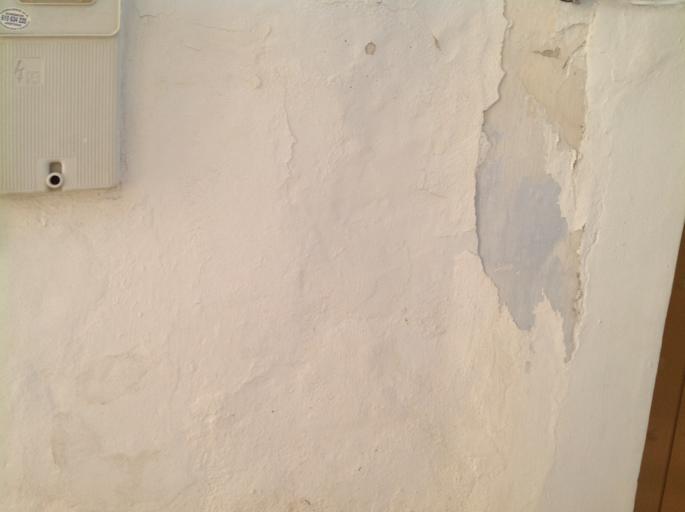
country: ES
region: Andalusia
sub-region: Provincia de Malaga
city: Frigiliana
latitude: 36.7921
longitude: -3.8977
